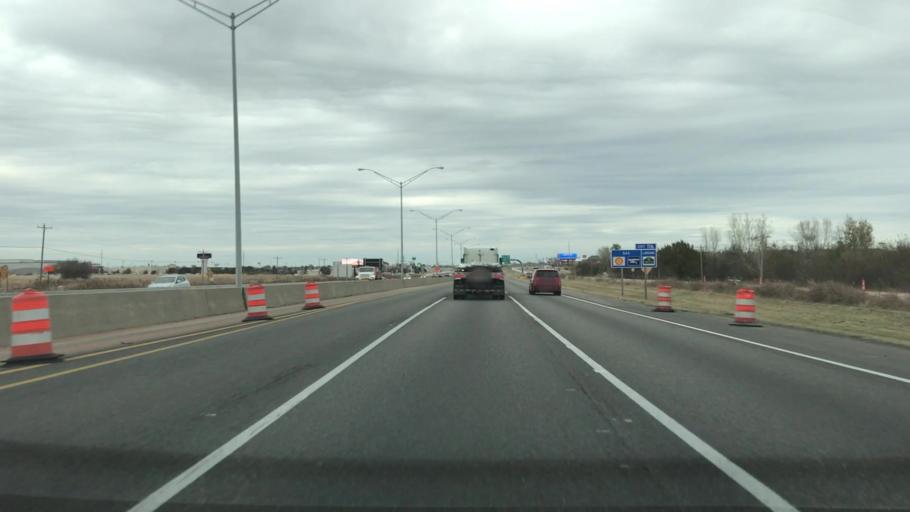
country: US
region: Oklahoma
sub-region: Cleveland County
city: Moore
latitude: 35.3062
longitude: -97.4899
